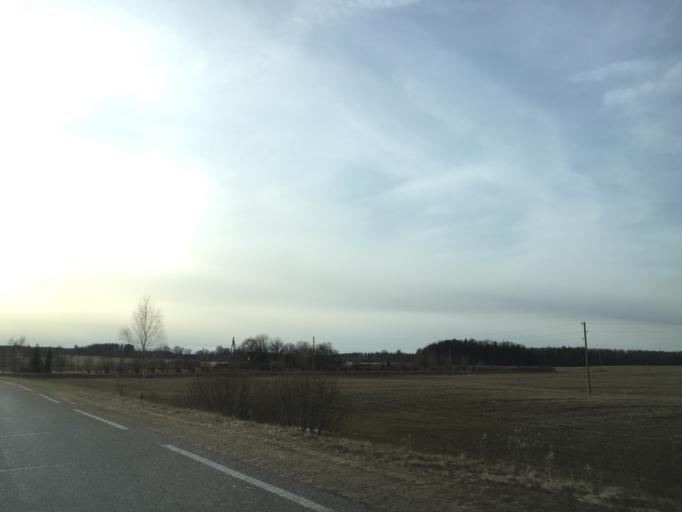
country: LV
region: Krimulda
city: Ragana
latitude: 57.1651
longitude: 24.7756
